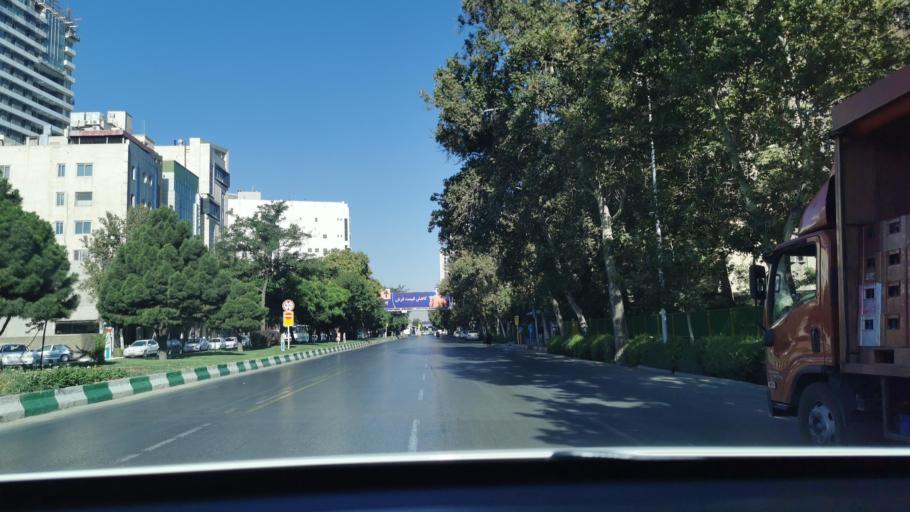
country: IR
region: Razavi Khorasan
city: Mashhad
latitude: 36.3240
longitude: 59.5740
